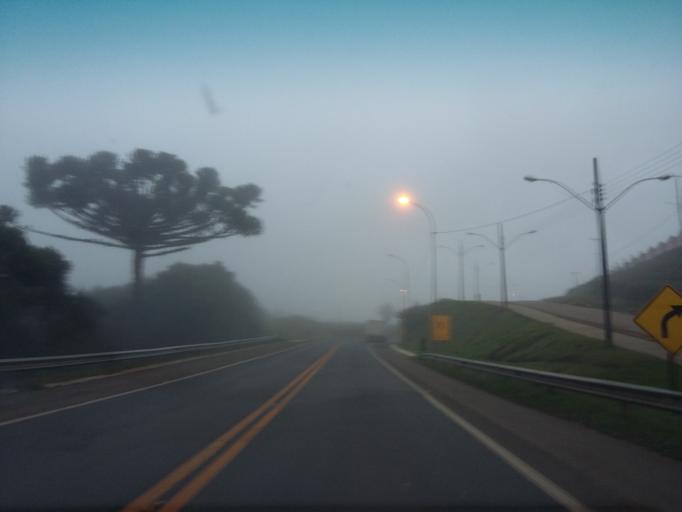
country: BR
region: Santa Catarina
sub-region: Curitibanos
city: Curitibanos
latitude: -27.2629
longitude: -50.4441
